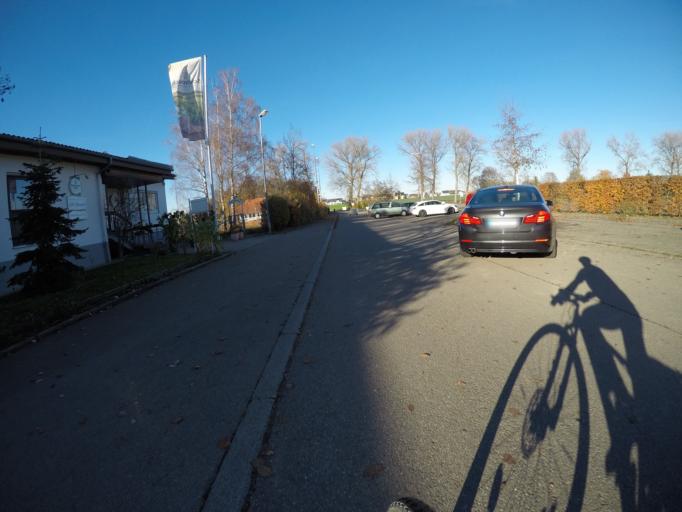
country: DE
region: Baden-Wuerttemberg
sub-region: Regierungsbezirk Stuttgart
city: Ehningen
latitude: 48.6819
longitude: 8.9579
